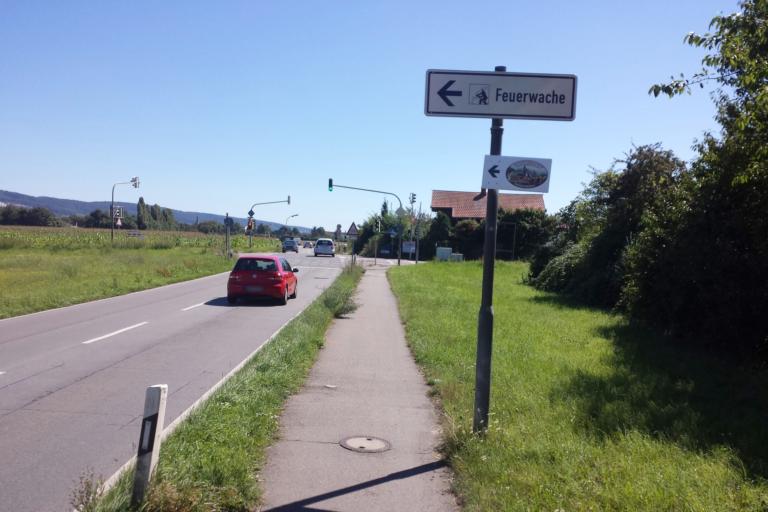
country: DE
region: Baden-Wuerttemberg
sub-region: Karlsruhe Region
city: Eppelheim
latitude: 49.3956
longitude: 8.6563
